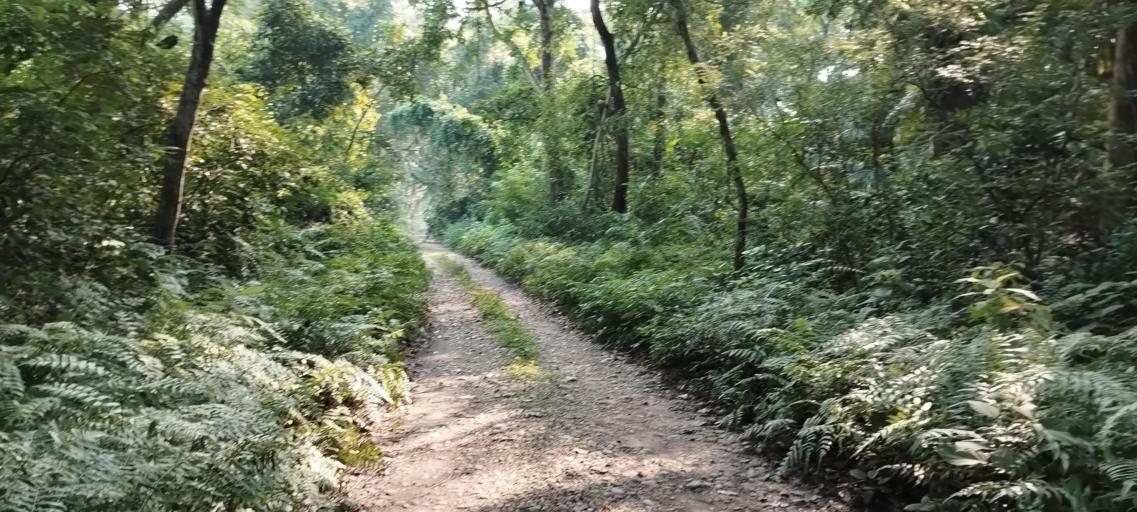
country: NP
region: Far Western
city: Tikapur
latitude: 28.4631
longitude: 81.2425
